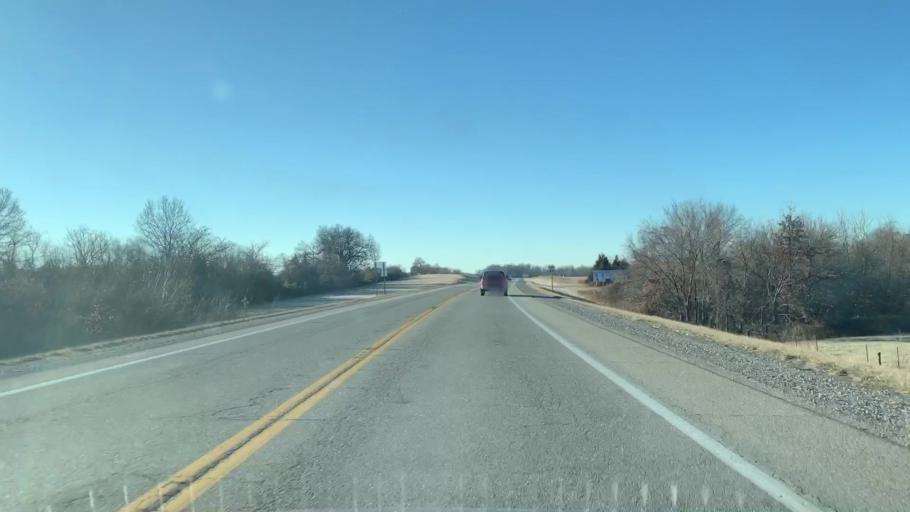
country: US
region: Kansas
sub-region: Crawford County
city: Arma
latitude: 37.5361
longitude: -94.7102
